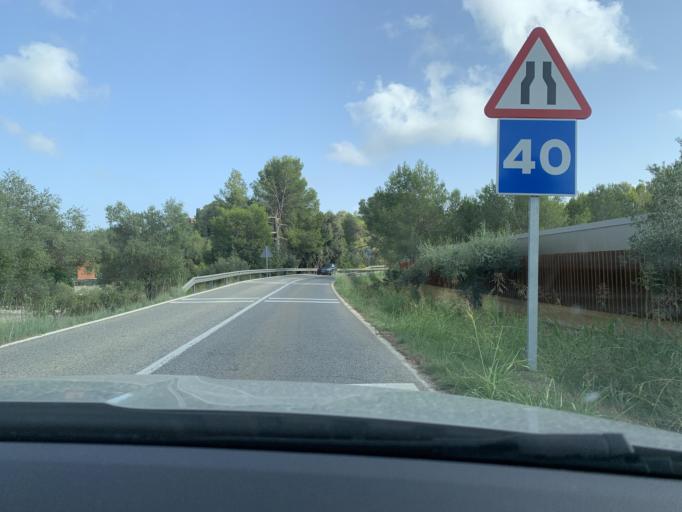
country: ES
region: Catalonia
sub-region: Provincia de Tarragona
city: el Catllar
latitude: 41.1518
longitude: 1.3150
